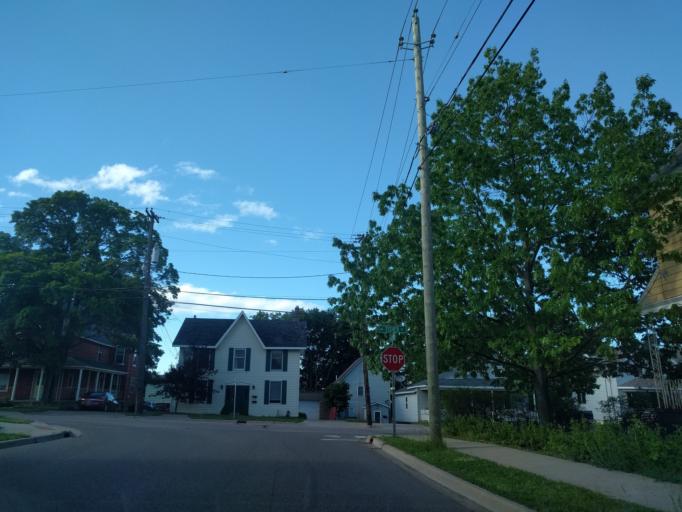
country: US
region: Michigan
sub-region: Marquette County
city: Marquette
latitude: 46.5388
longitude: -87.3958
